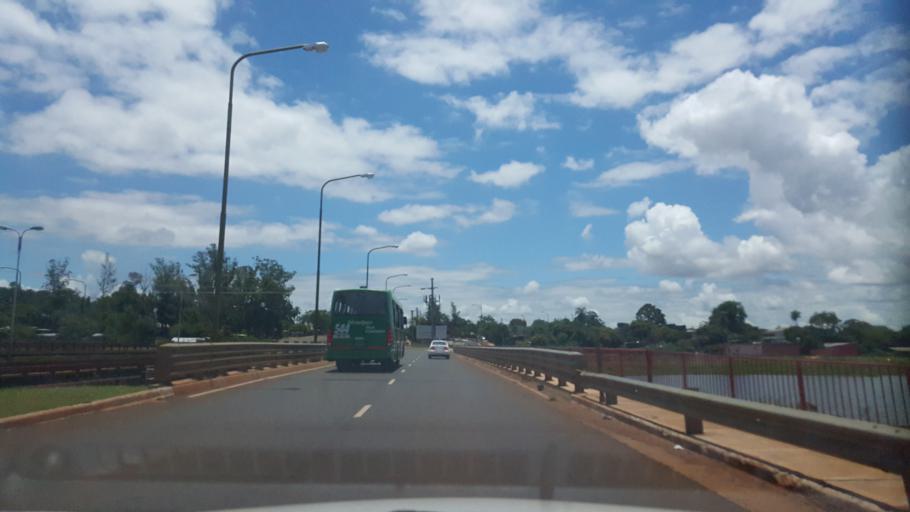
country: AR
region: Misiones
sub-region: Departamento de Capital
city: Posadas
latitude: -27.4191
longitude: -55.8996
